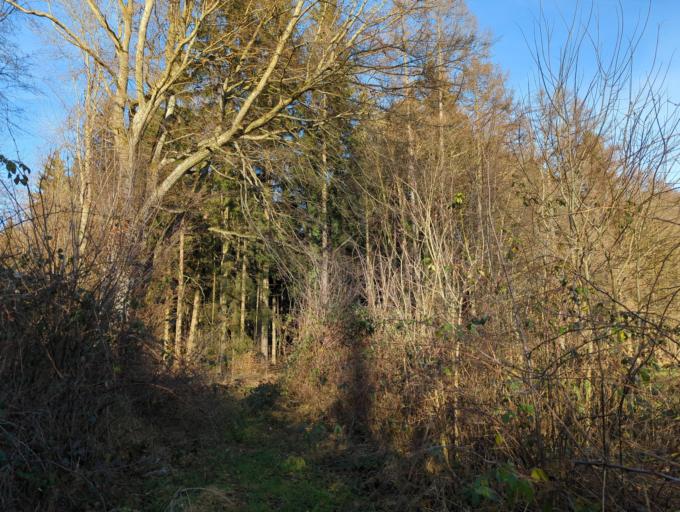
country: DE
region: Bavaria
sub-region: Swabia
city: Krumbach
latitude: 48.2519
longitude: 10.3976
